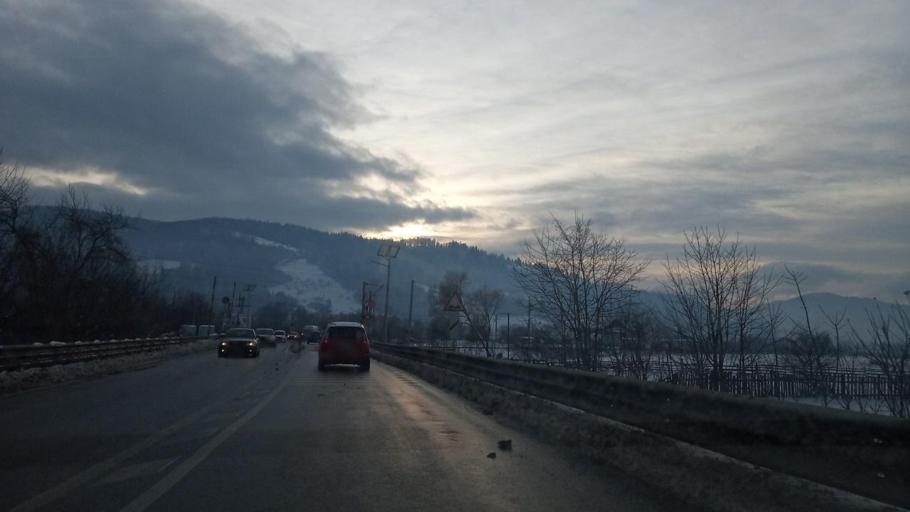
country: RO
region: Suceava
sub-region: Comuna Frasin
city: Bucsoaia
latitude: 47.5433
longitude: 25.8419
